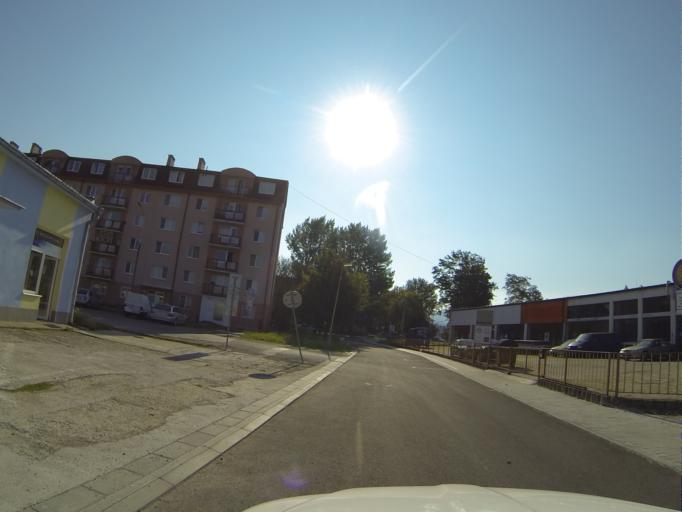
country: SK
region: Nitriansky
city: Prievidza
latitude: 48.7695
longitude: 18.6242
